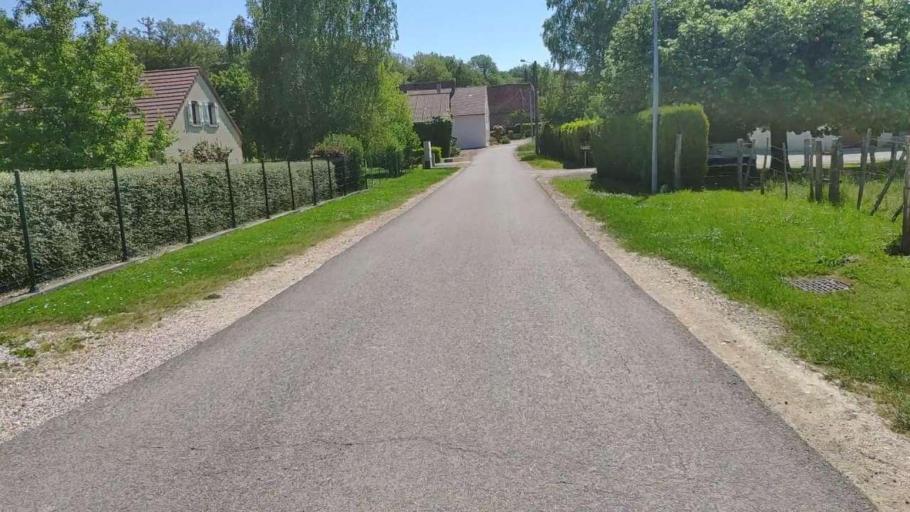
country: FR
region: Franche-Comte
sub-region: Departement du Jura
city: Bletterans
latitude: 46.7661
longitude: 5.4335
